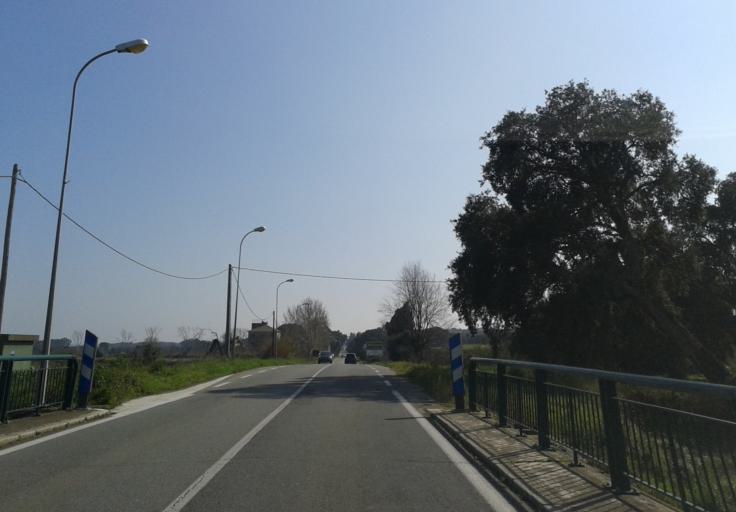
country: FR
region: Corsica
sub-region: Departement de la Haute-Corse
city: Cervione
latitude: 42.3123
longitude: 9.5419
